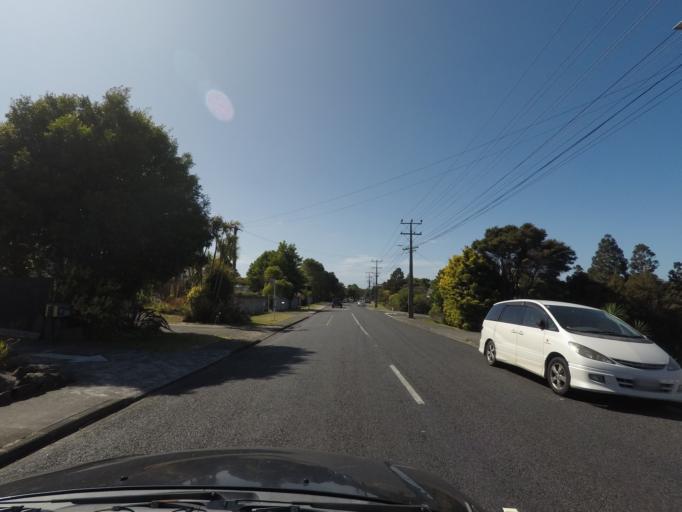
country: NZ
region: Auckland
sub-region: Auckland
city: Titirangi
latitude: -36.9294
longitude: 174.6549
